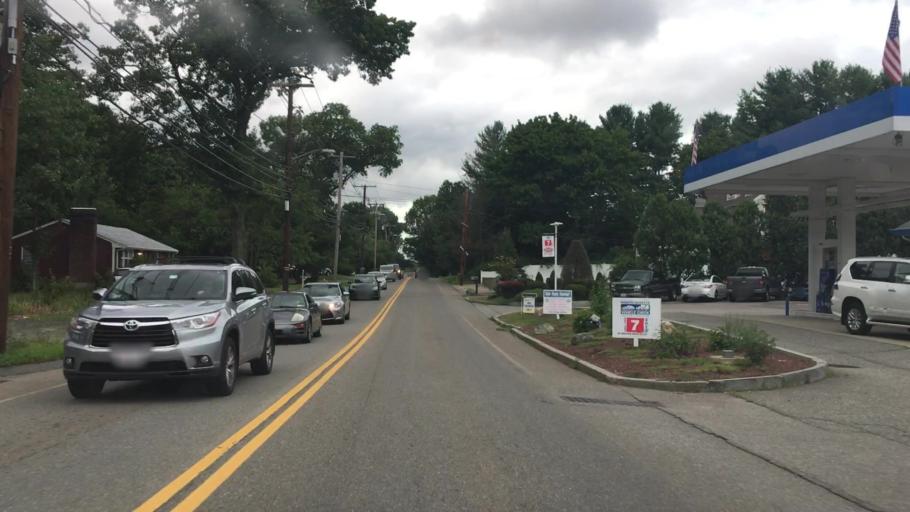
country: US
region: Massachusetts
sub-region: Middlesex County
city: Lexington
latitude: 42.4659
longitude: -71.2082
